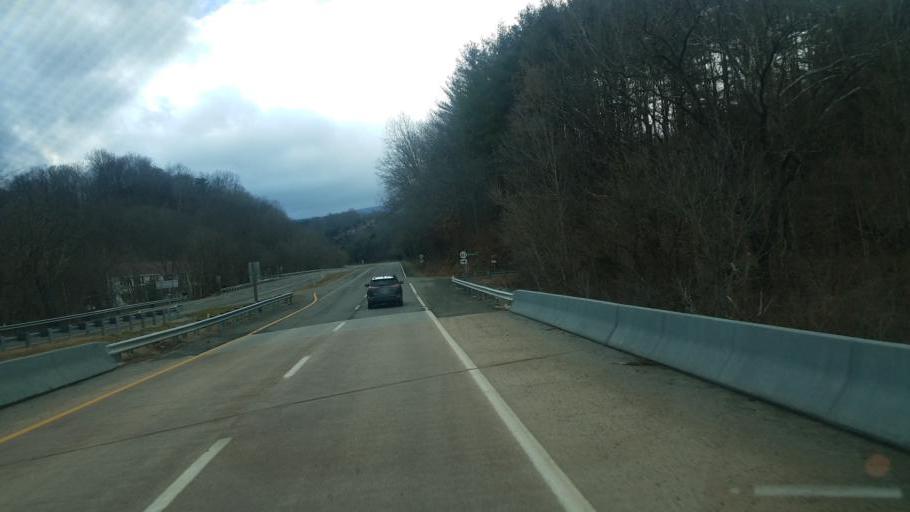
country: US
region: Virginia
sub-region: Giles County
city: Pearisburg
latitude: 37.2670
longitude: -80.7120
